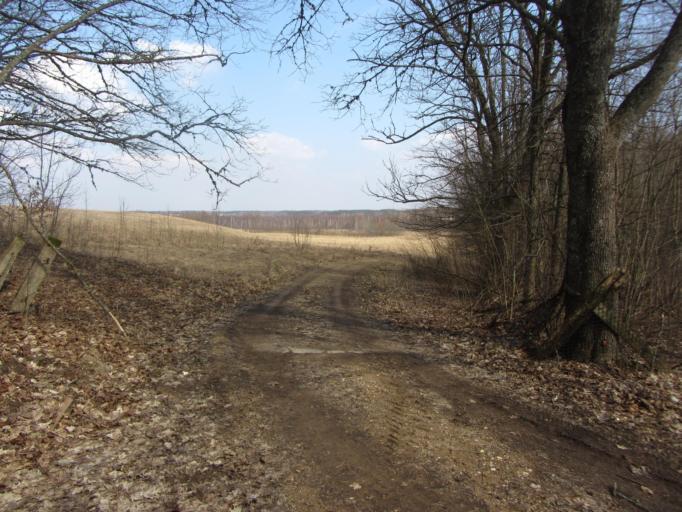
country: LT
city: Dukstas
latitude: 55.5405
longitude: 26.2473
